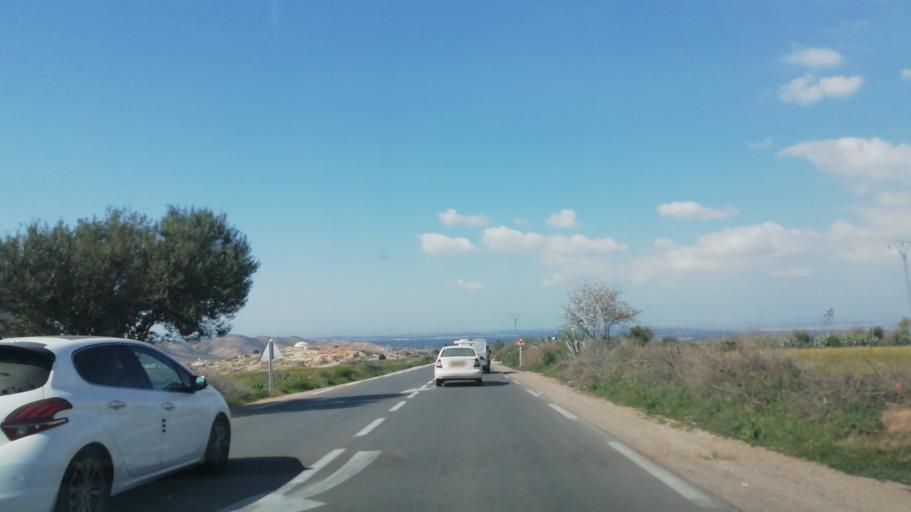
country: DZ
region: Mascara
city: Mascara
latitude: 35.5509
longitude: 0.0848
